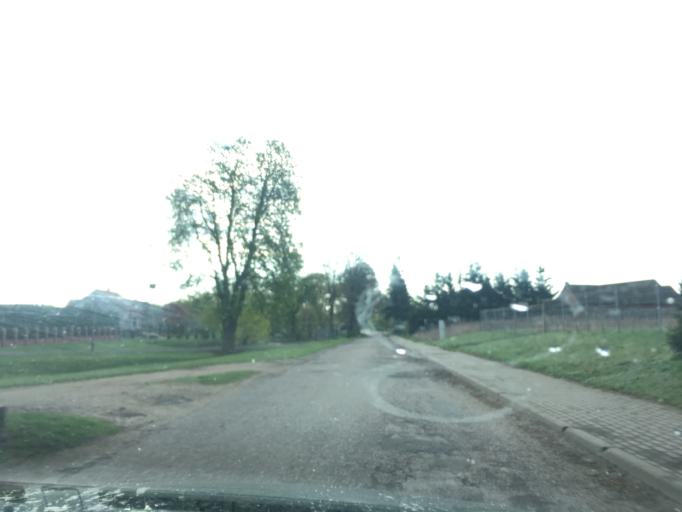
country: PL
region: Warmian-Masurian Voivodeship
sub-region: Powiat ostrodzki
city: Dabrowno
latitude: 53.4376
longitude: 19.9834
